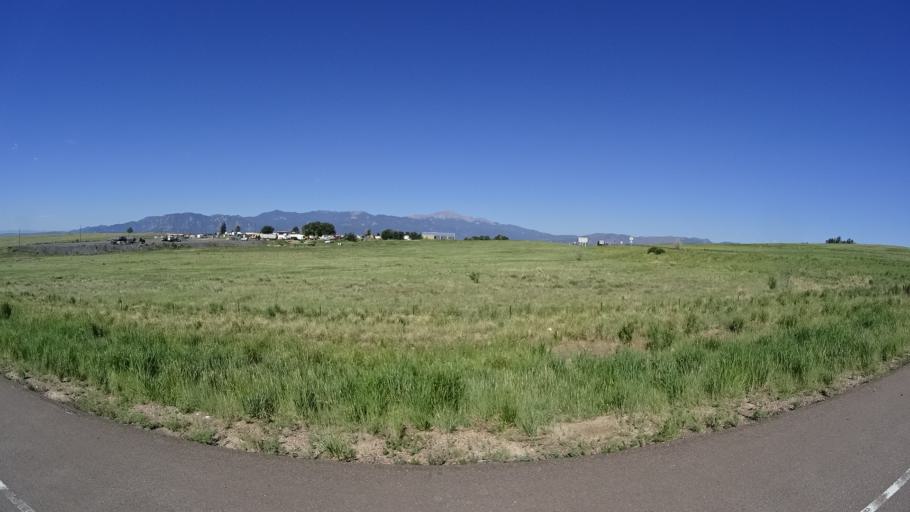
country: US
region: Colorado
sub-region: El Paso County
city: Cimarron Hills
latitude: 38.8410
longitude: -104.6828
